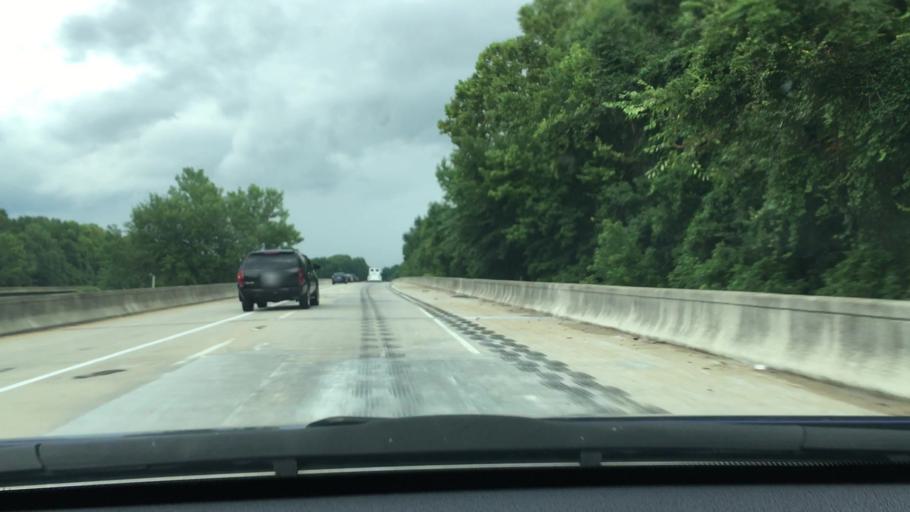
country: US
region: South Carolina
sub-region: Sumter County
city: Stateburg
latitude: 33.9468
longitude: -80.6297
